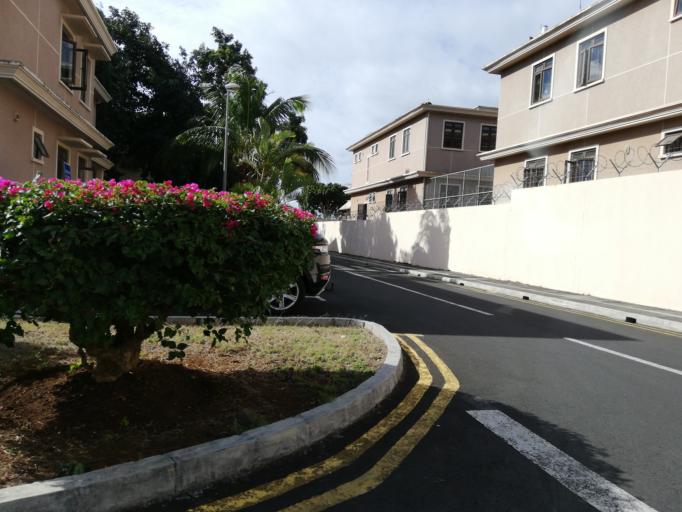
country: MU
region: Plaines Wilhems
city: Ebene
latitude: -20.2287
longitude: 57.4603
